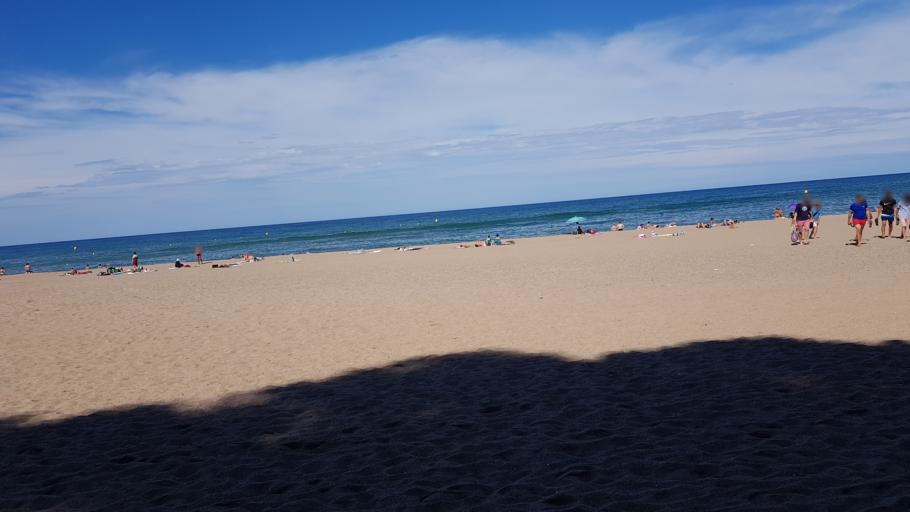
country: ES
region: Catalonia
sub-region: Provincia de Girona
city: Begur
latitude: 41.9791
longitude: 3.2084
